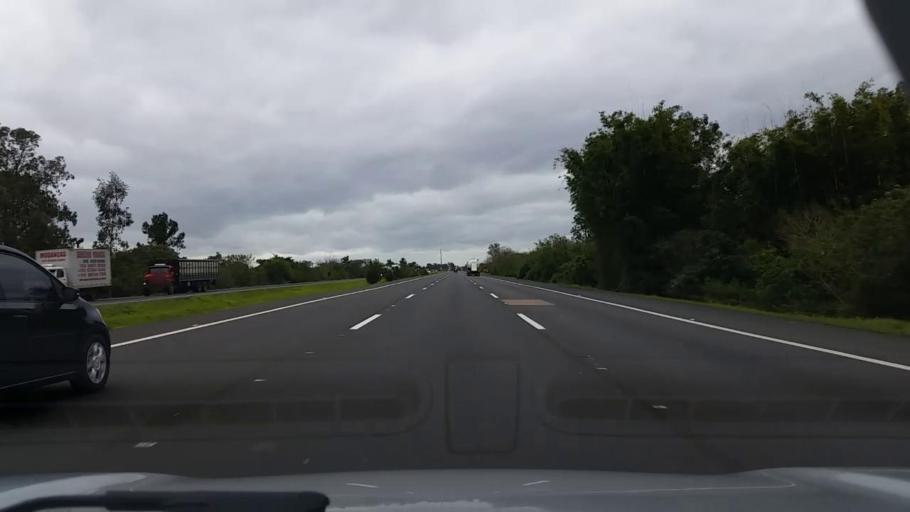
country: BR
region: Rio Grande do Sul
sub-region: Rolante
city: Rolante
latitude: -29.8836
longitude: -50.5562
